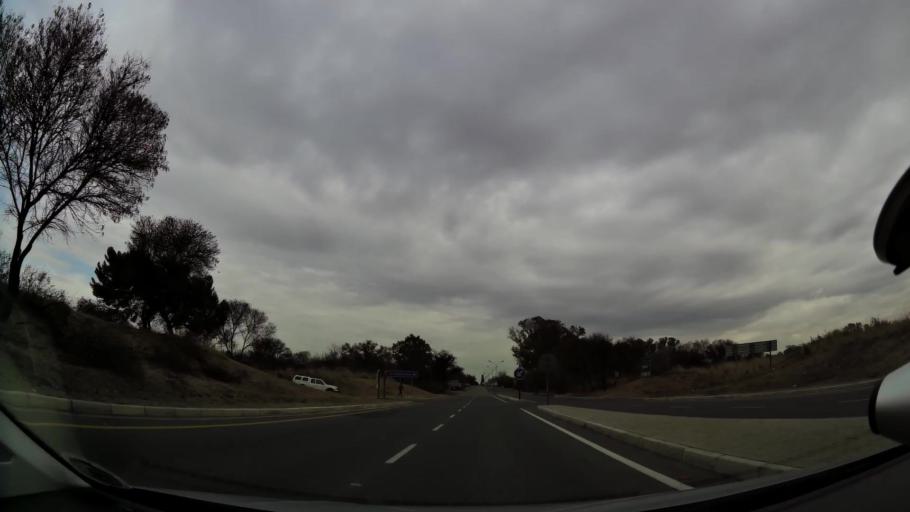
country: ZA
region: Orange Free State
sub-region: Fezile Dabi District Municipality
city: Kroonstad
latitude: -27.6571
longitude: 27.2495
